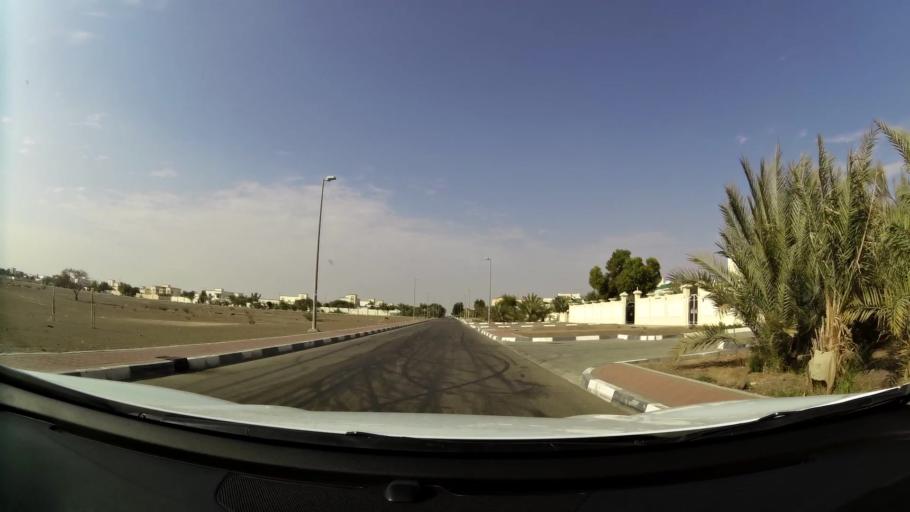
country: AE
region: Abu Dhabi
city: Al Ain
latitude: 24.0801
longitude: 55.8685
